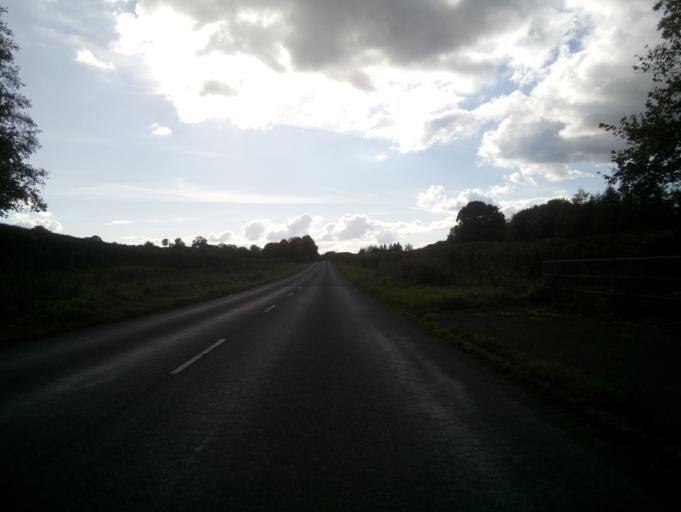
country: GB
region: Wales
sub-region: Sir Powys
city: Hay
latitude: 52.0580
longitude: -3.1648
